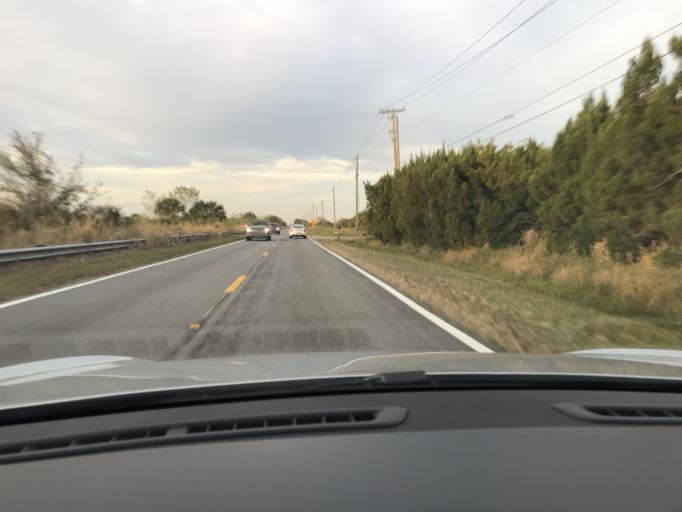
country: US
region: Florida
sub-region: Saint Lucie County
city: Lakewood Park
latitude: 27.5481
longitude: -80.4309
